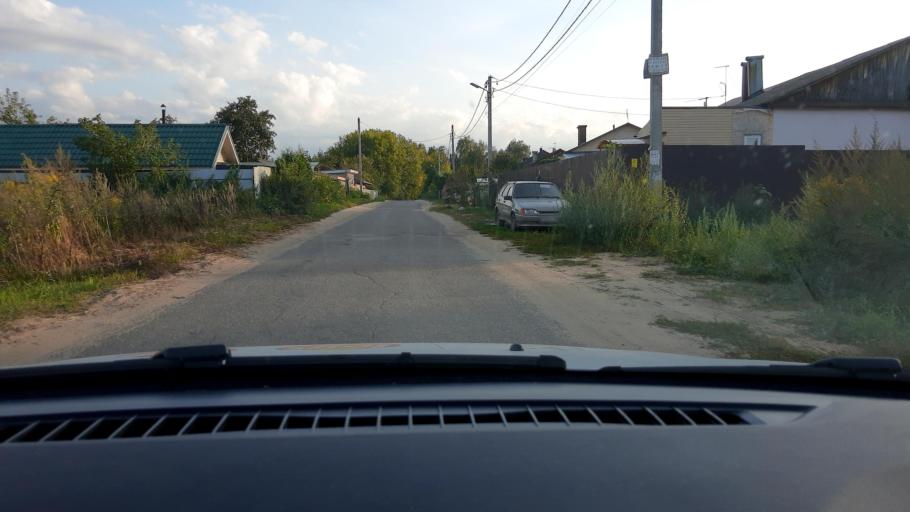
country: RU
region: Nizjnij Novgorod
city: Sitniki
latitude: 56.4148
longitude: 44.0386
